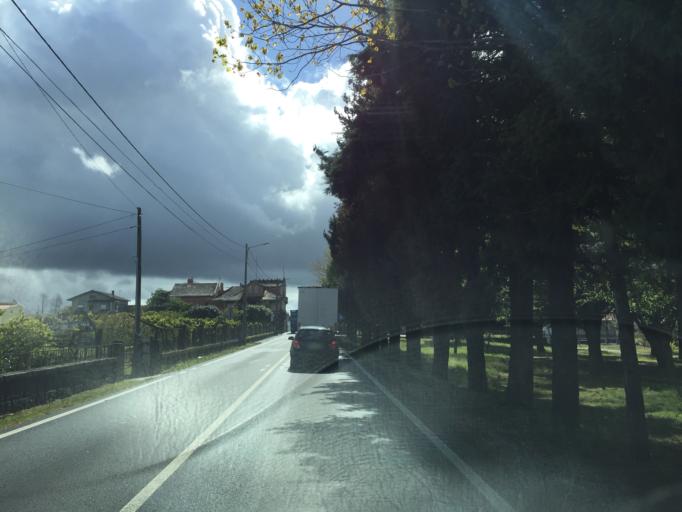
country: PT
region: Coimbra
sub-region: Oliveira do Hospital
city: Oliveira do Hospital
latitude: 40.3334
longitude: -7.8663
